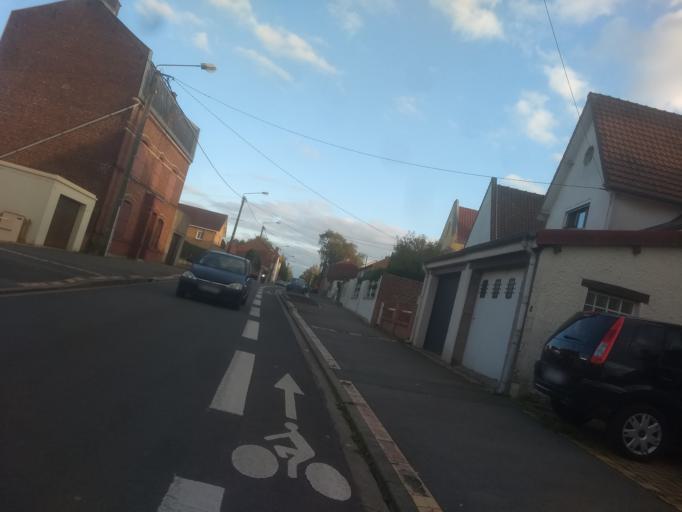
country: FR
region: Nord-Pas-de-Calais
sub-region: Departement du Pas-de-Calais
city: Arras
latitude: 50.2819
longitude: 2.7901
